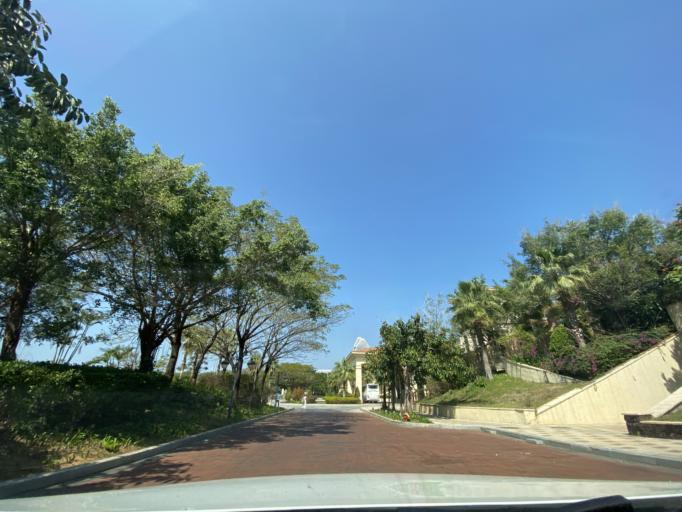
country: CN
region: Hainan
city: Haitangwan
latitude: 18.3491
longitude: 109.7355
